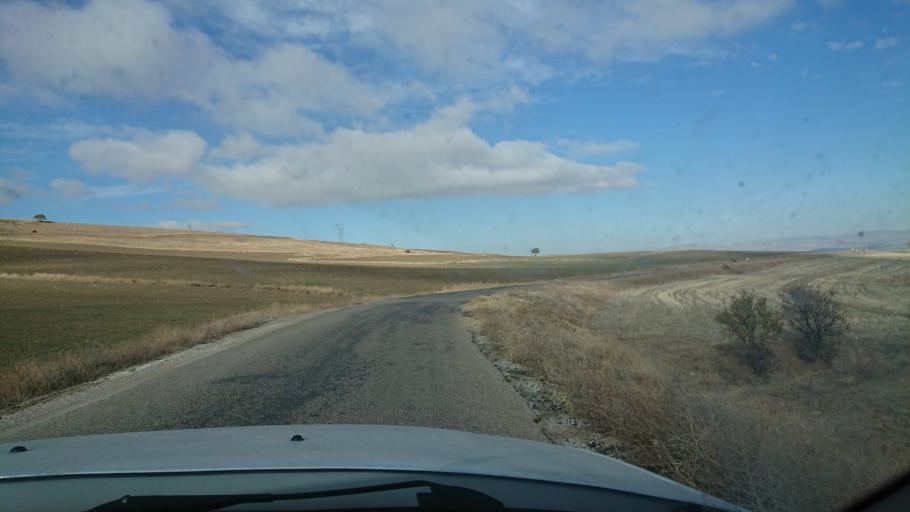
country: TR
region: Aksaray
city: Agacoren
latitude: 38.8443
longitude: 33.9501
